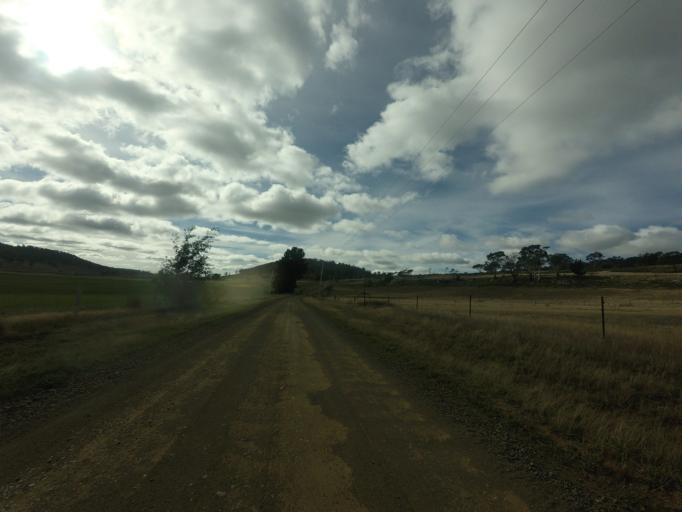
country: AU
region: Tasmania
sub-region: Brighton
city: Bridgewater
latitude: -42.3919
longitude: 147.3978
